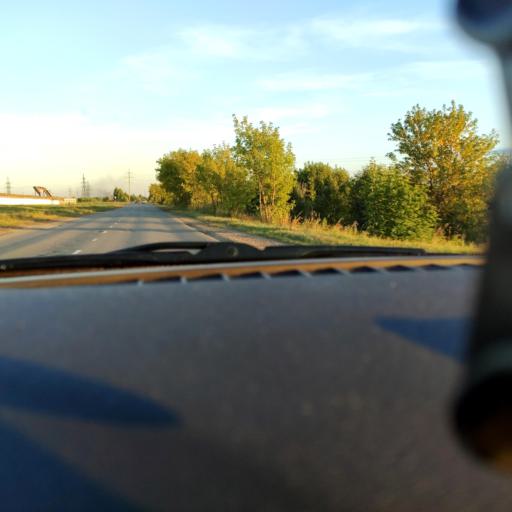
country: RU
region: Perm
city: Gamovo
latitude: 57.9150
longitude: 56.1110
